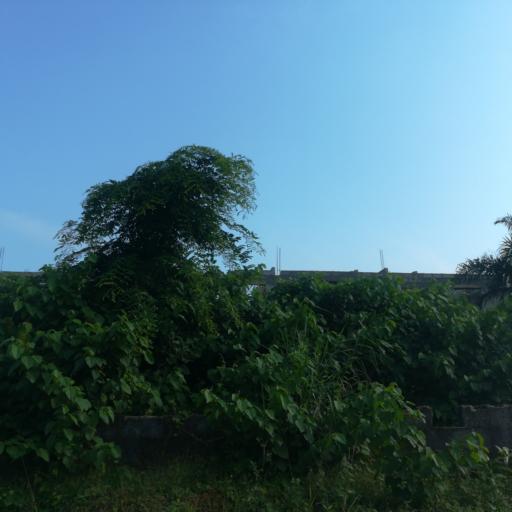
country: NG
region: Rivers
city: Port Harcourt
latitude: 4.8503
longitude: 6.9602
